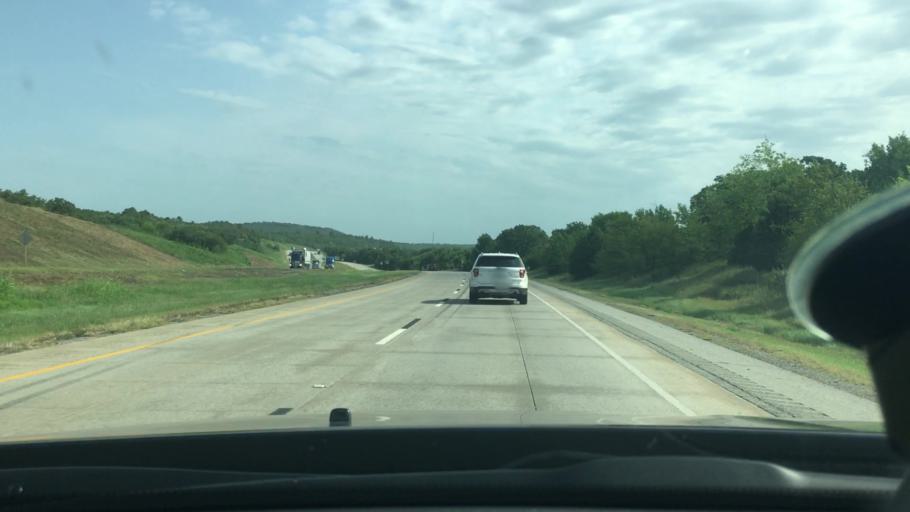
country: US
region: Oklahoma
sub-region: Atoka County
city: Atoka
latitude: 34.4419
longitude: -96.0726
